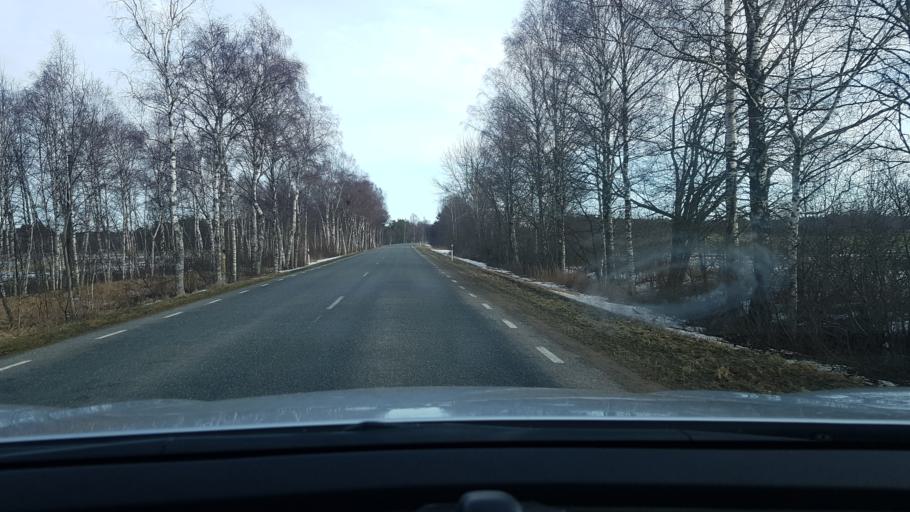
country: EE
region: Saare
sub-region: Kuressaare linn
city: Kuressaare
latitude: 58.4261
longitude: 22.6760
